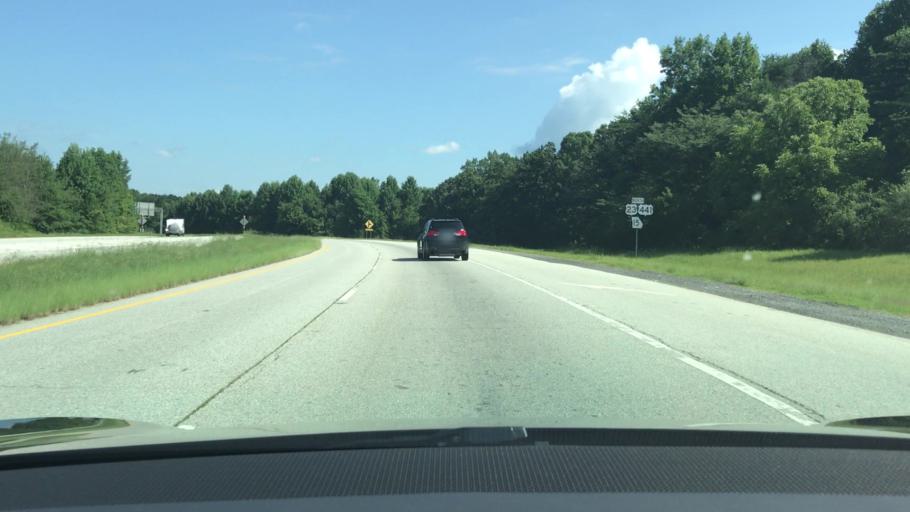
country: US
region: Georgia
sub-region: Habersham County
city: Clarkesville
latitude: 34.5954
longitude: -83.4412
